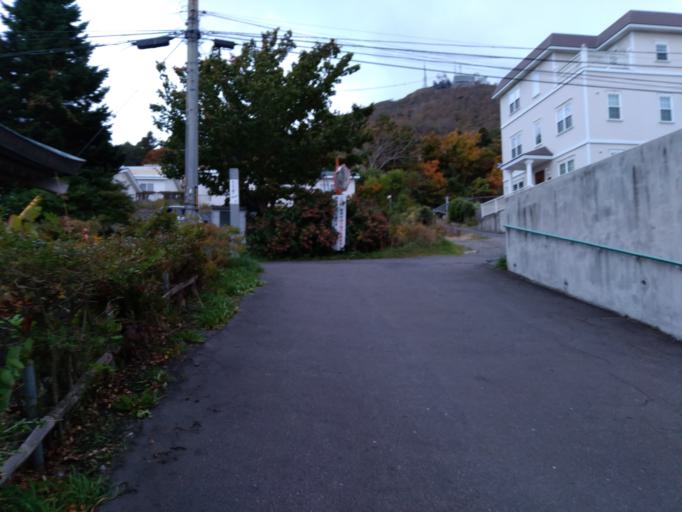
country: JP
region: Hokkaido
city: Hakodate
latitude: 41.7622
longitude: 140.7121
